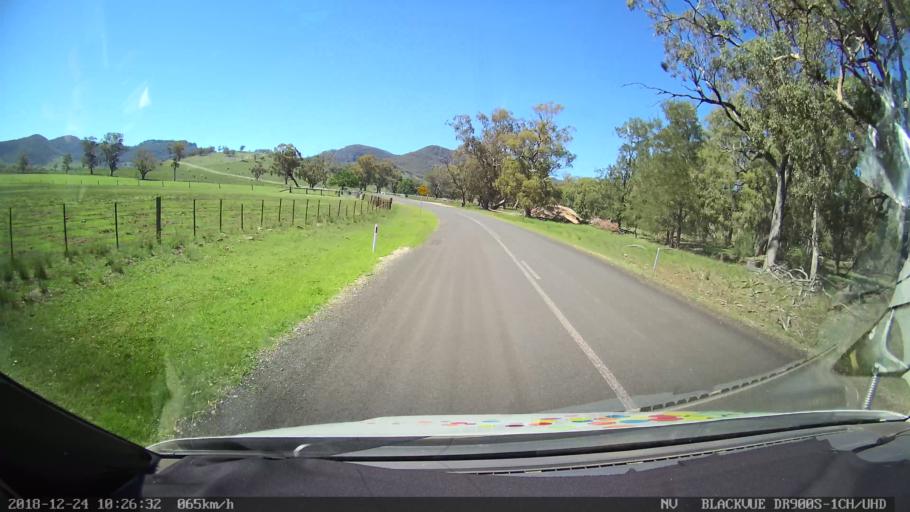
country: AU
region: New South Wales
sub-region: Liverpool Plains
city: Quirindi
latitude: -31.8102
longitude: 150.5273
